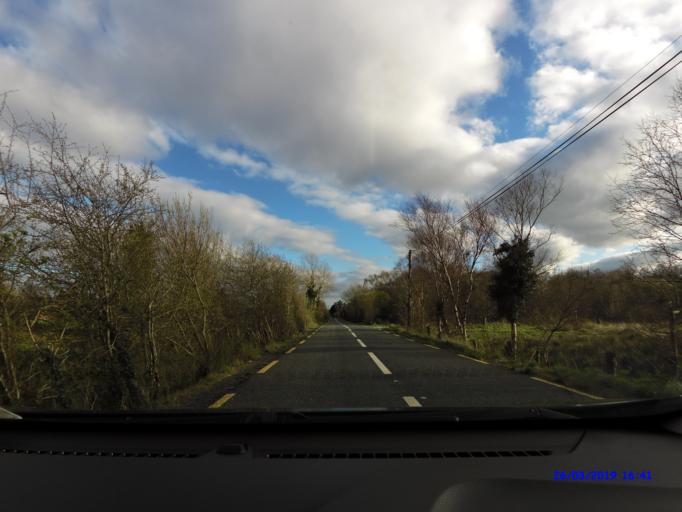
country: IE
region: Connaught
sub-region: Maigh Eo
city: Ballyhaunis
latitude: 53.8745
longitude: -8.7740
